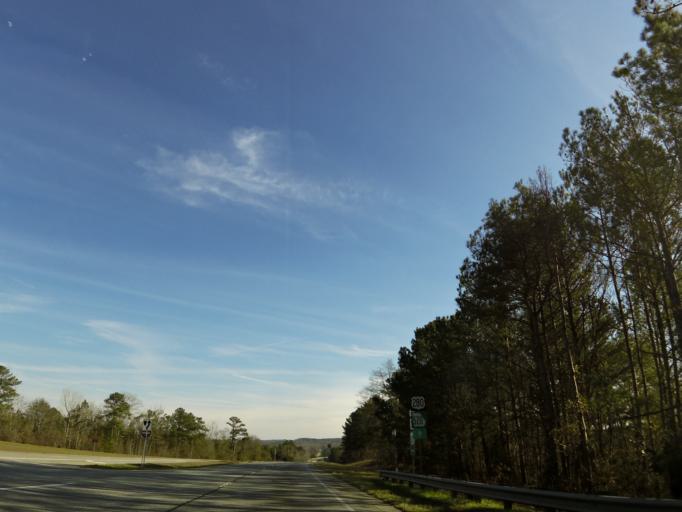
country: US
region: Georgia
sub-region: Chattahoochee County
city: Cusseta
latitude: 32.2909
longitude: -84.7680
